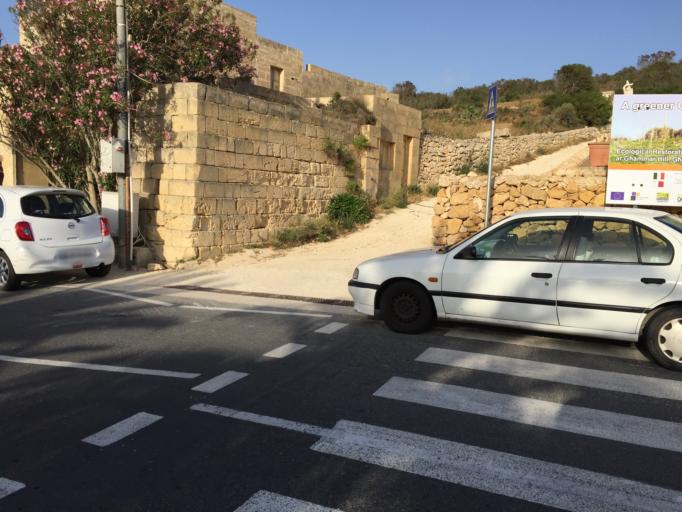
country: MT
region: L-Gharb
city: Gharb
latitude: 36.0613
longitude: 14.2160
